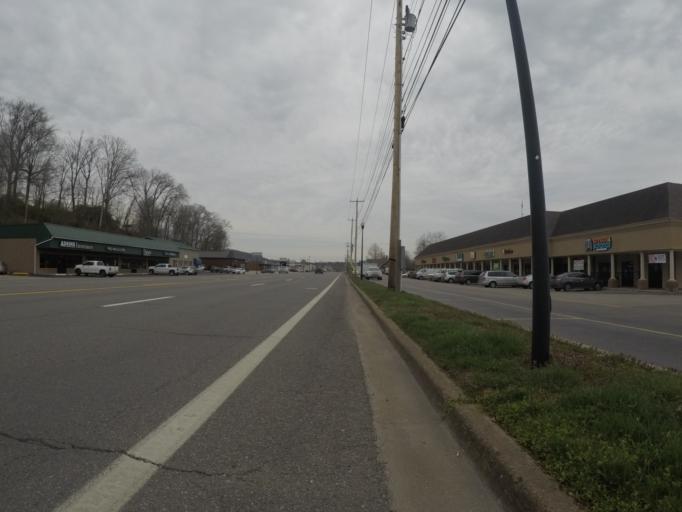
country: US
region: West Virginia
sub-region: Cabell County
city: Pea Ridge
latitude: 38.4130
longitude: -82.3095
